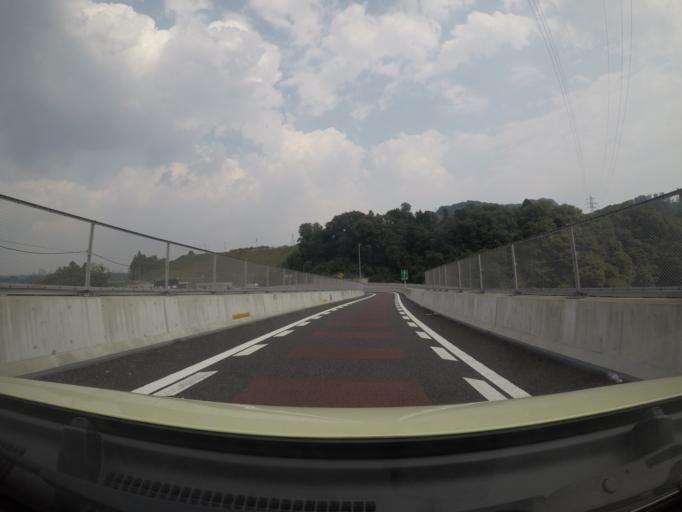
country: JP
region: Tokyo
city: Hachioji
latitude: 35.5801
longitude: 139.2894
